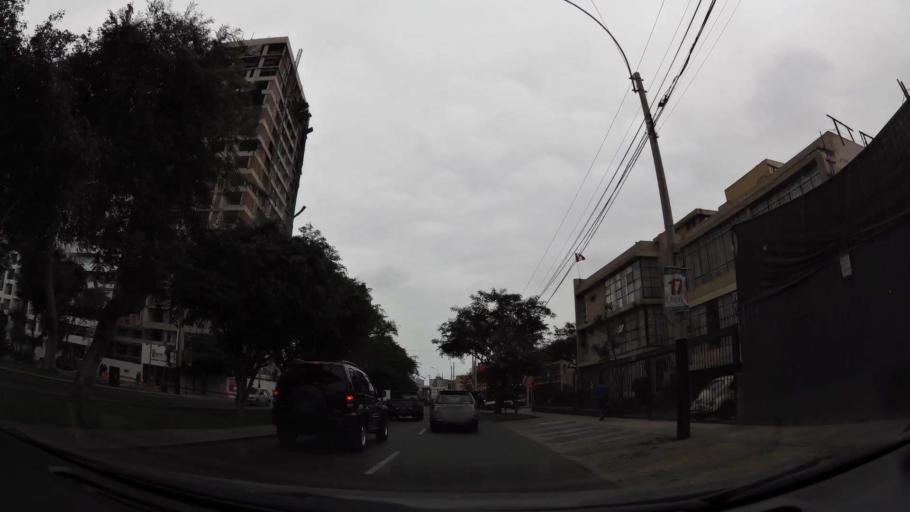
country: PE
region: Lima
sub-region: Lima
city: San Isidro
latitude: -12.0876
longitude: -77.0441
